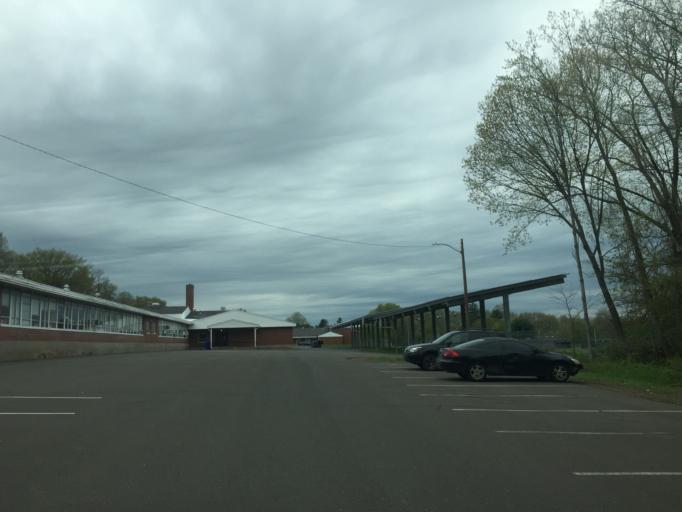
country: US
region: Connecticut
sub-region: Hartford County
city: Glastonbury
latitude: 41.7359
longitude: -72.5894
